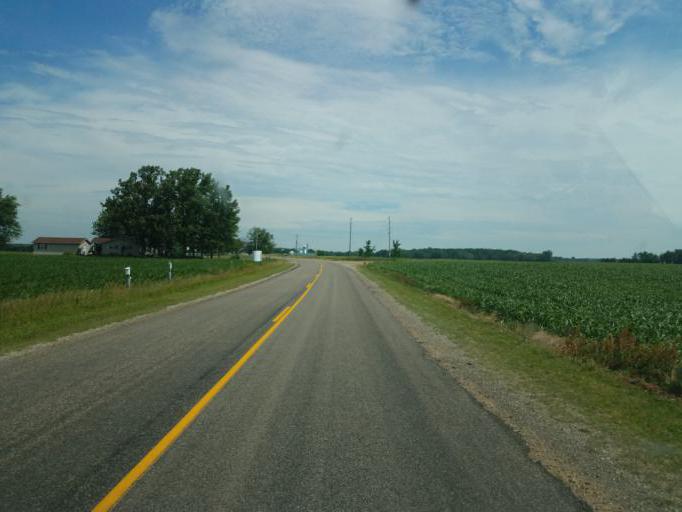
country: US
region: Michigan
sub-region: Barry County
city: Nashville
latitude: 42.6390
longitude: -85.0247
